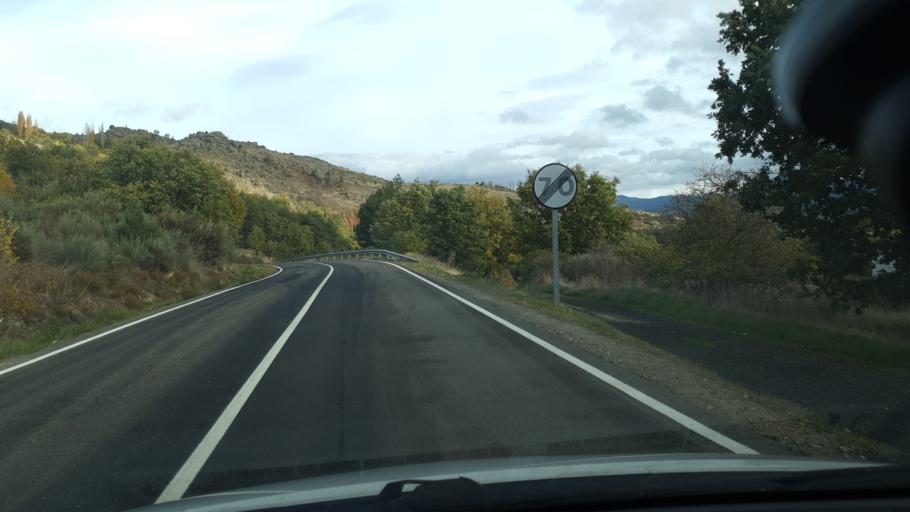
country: ES
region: Castille and Leon
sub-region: Provincia de Avila
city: Hoyocasero
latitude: 40.3971
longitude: -4.9731
